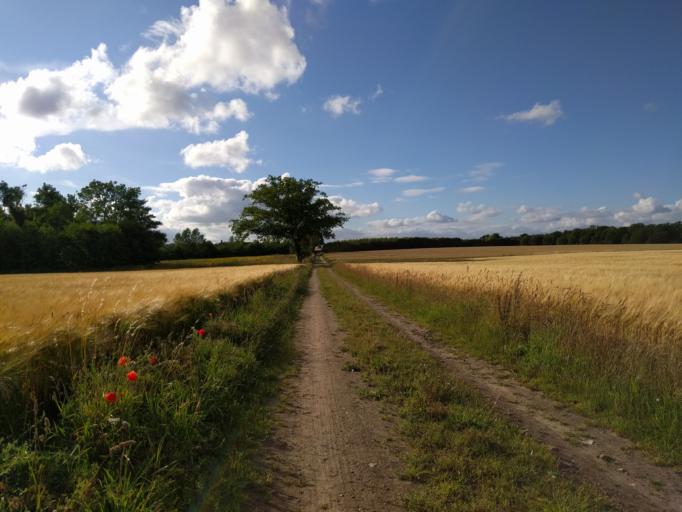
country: DK
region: South Denmark
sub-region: Kerteminde Kommune
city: Langeskov
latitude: 55.3877
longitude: 10.5513
